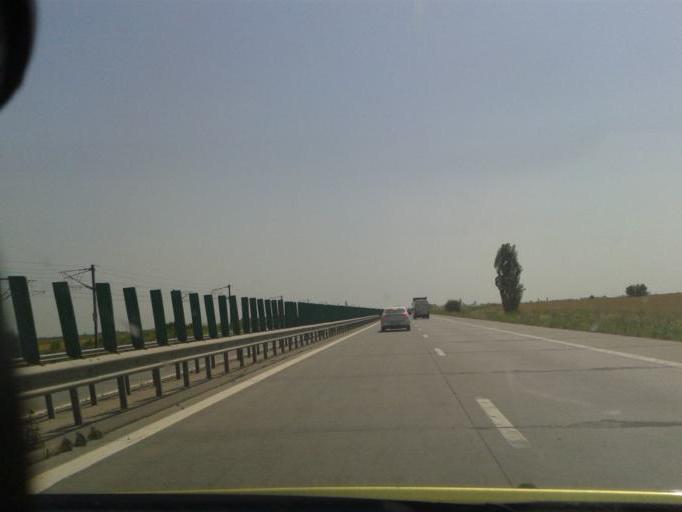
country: RO
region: Calarasi
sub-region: Comuna Belciugatele
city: Belciugatele
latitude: 44.4554
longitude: 26.4695
